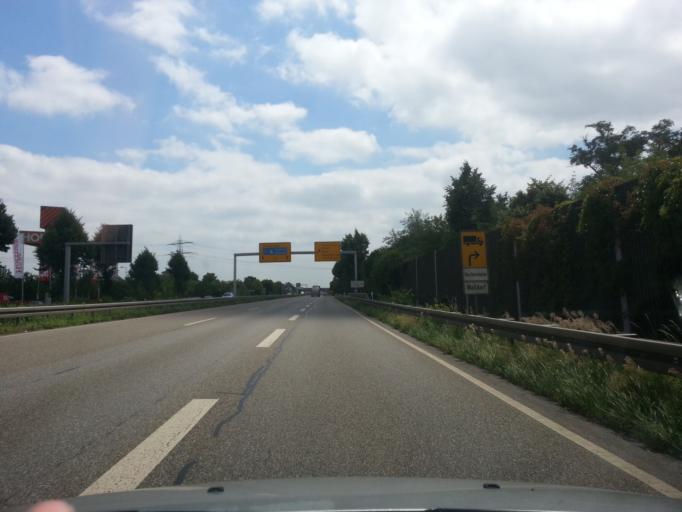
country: DE
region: Baden-Wuerttemberg
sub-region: Karlsruhe Region
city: Bruhl
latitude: 49.4144
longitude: 8.5419
